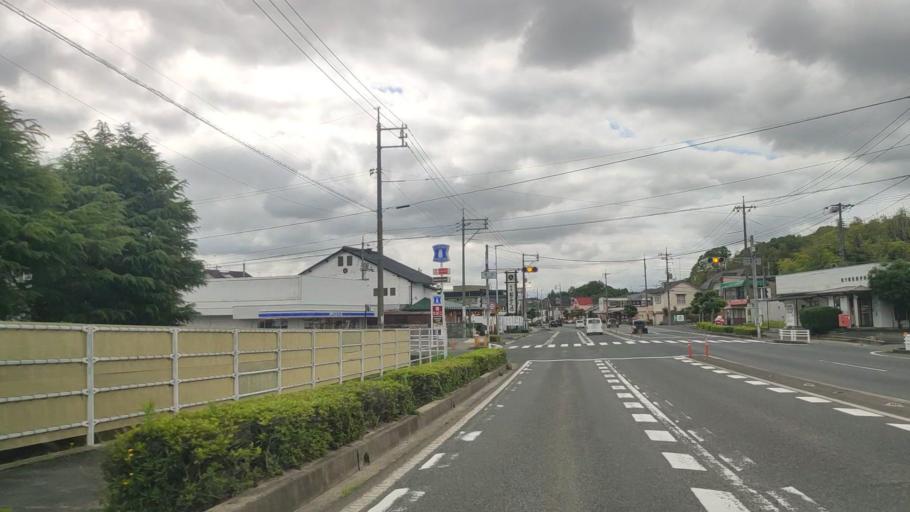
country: JP
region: Tottori
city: Yonago
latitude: 35.4069
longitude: 133.3650
